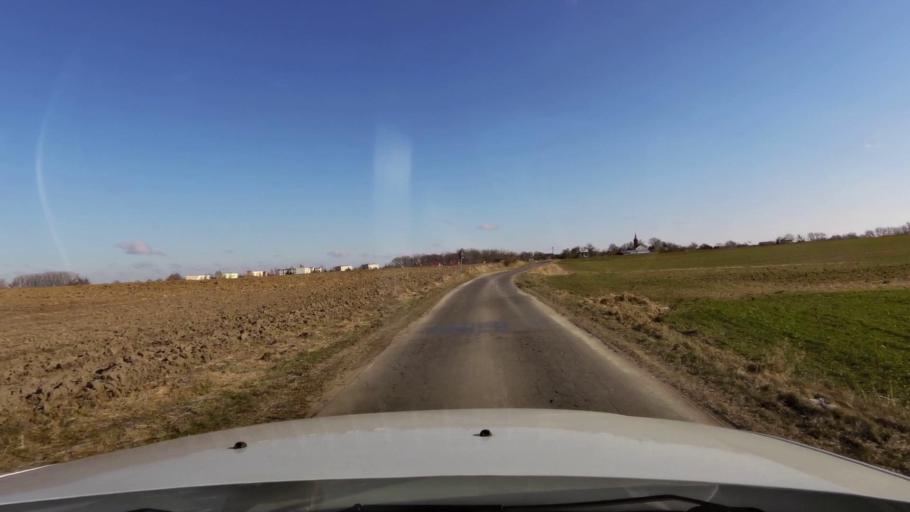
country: PL
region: West Pomeranian Voivodeship
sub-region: Powiat pyrzycki
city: Lipiany
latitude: 52.9888
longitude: 15.0461
